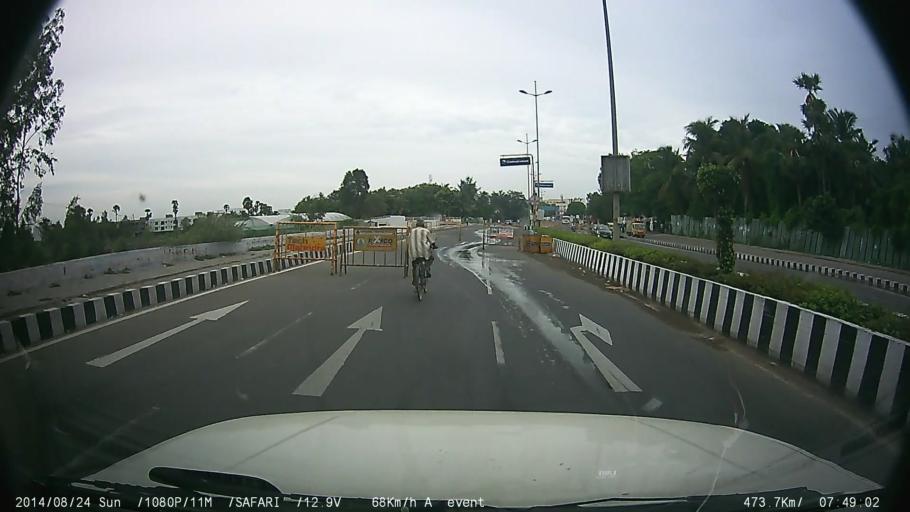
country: IN
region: Tamil Nadu
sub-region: Kancheepuram
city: Injambakkam
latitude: 12.8575
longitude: 80.2262
